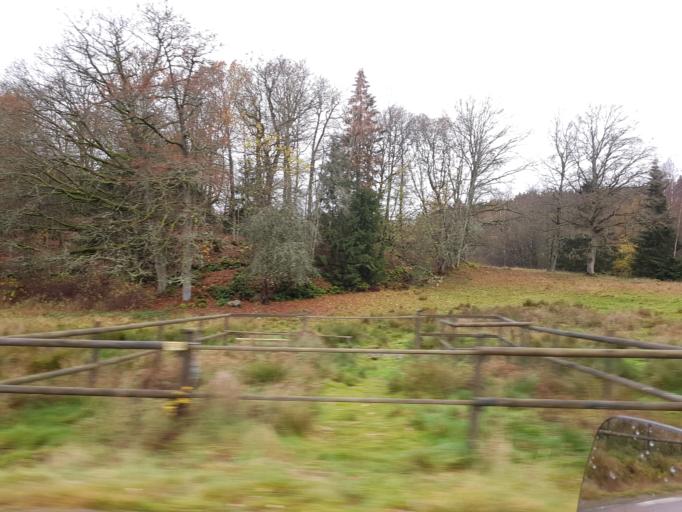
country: SE
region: Vaestra Goetaland
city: Svanesund
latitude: 58.1896
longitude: 11.8292
